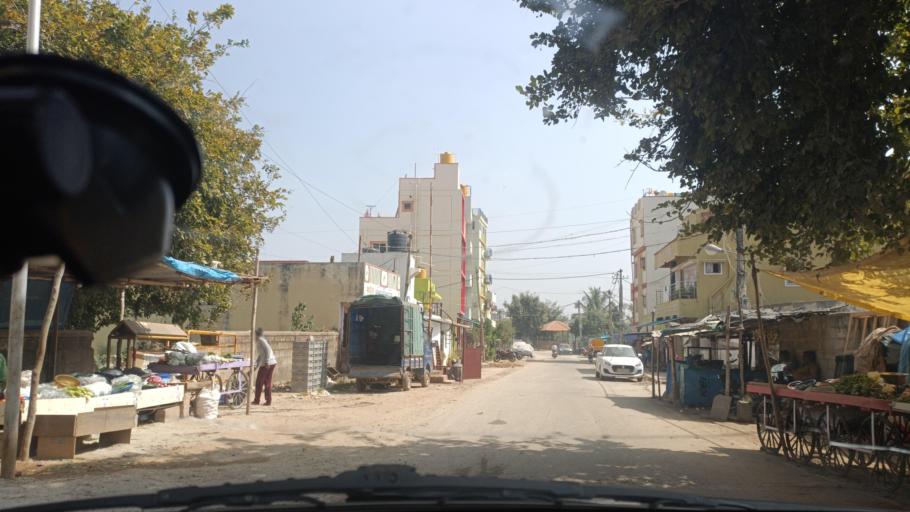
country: IN
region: Karnataka
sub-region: Bangalore Urban
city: Yelahanka
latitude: 13.1165
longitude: 77.6143
